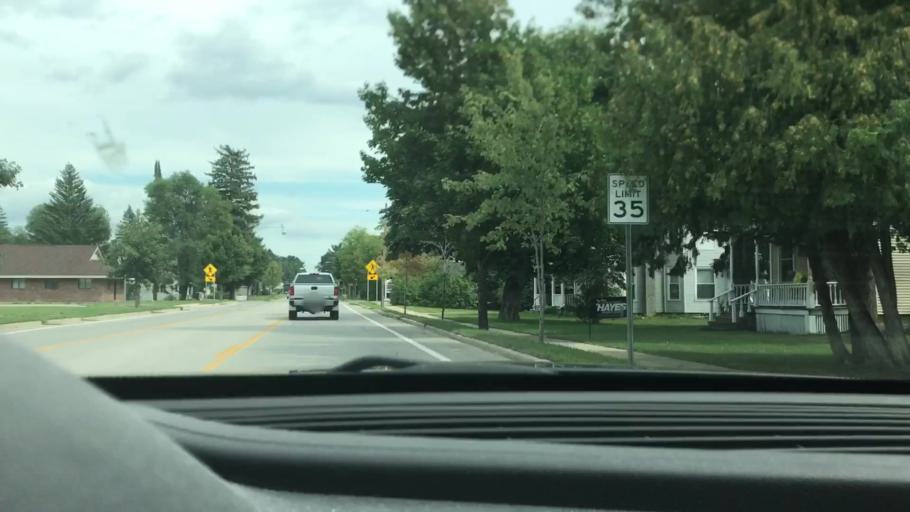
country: US
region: Michigan
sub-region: Antrim County
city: Bellaire
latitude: 44.9755
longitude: -85.2071
